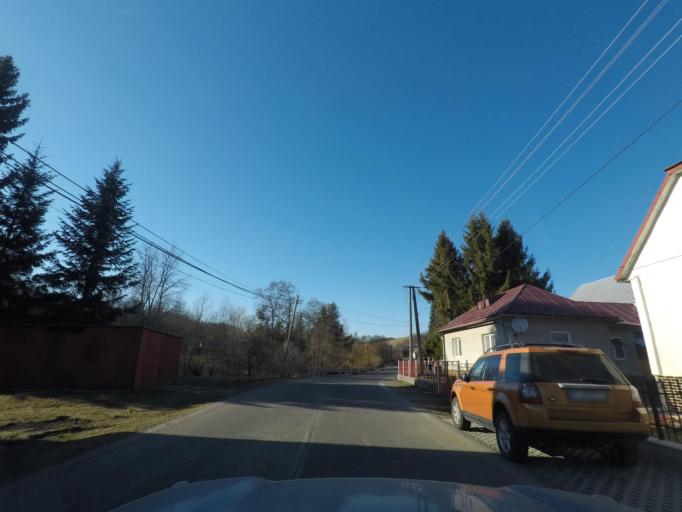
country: SK
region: Presovsky
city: Medzilaborce
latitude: 49.1927
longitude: 22.0033
